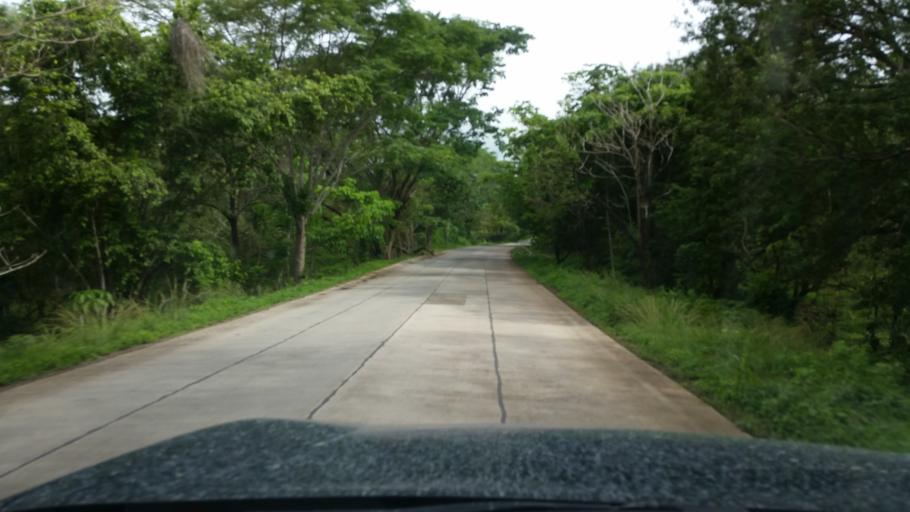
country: NI
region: Atlantico Norte (RAAN)
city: Siuna
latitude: 13.5578
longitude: -84.8182
